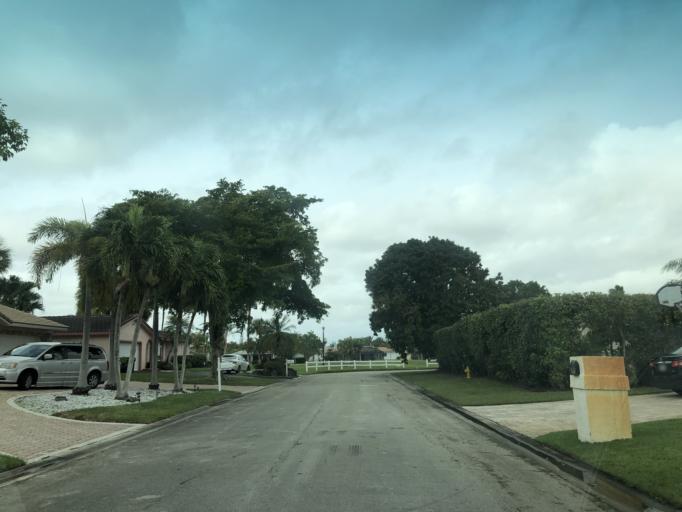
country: US
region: Florida
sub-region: Broward County
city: Margate
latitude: 26.2523
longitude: -80.2357
